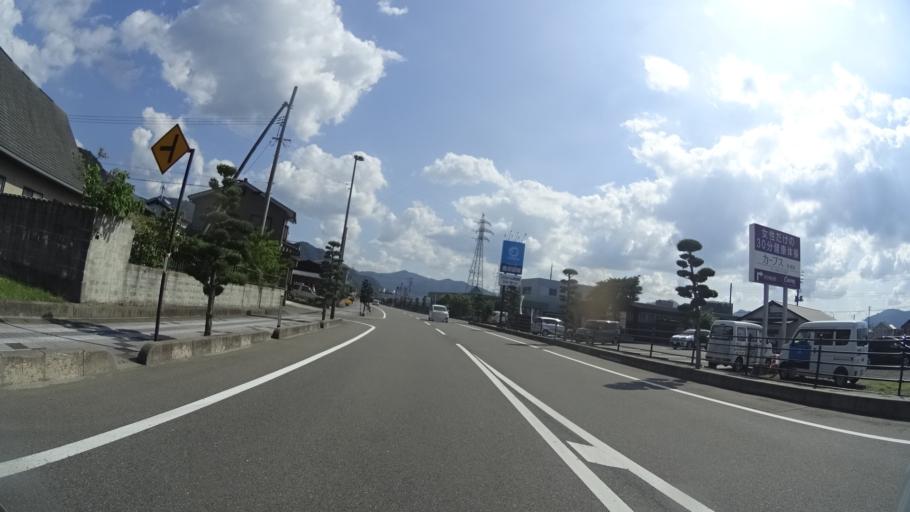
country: JP
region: Yamaguchi
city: Hagi
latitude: 34.4207
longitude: 131.4126
